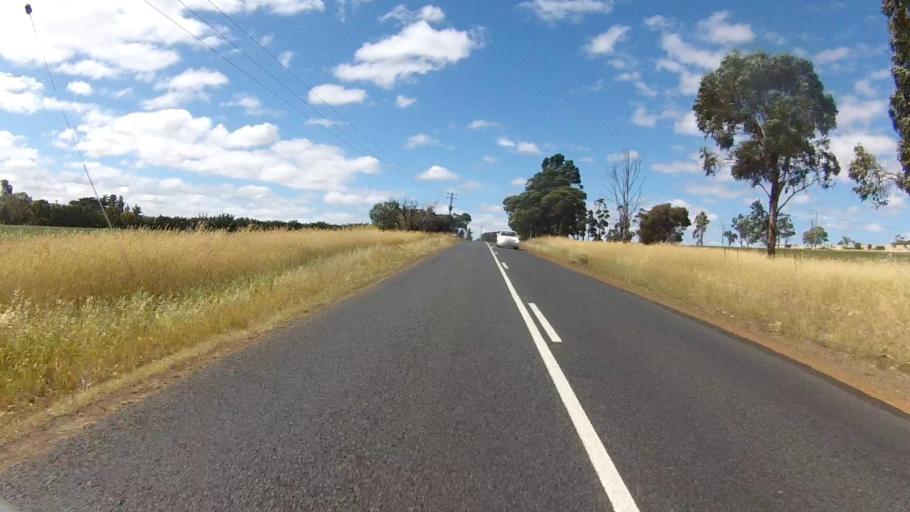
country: AU
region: Tasmania
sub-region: Sorell
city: Sorell
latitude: -42.6095
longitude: 147.4246
